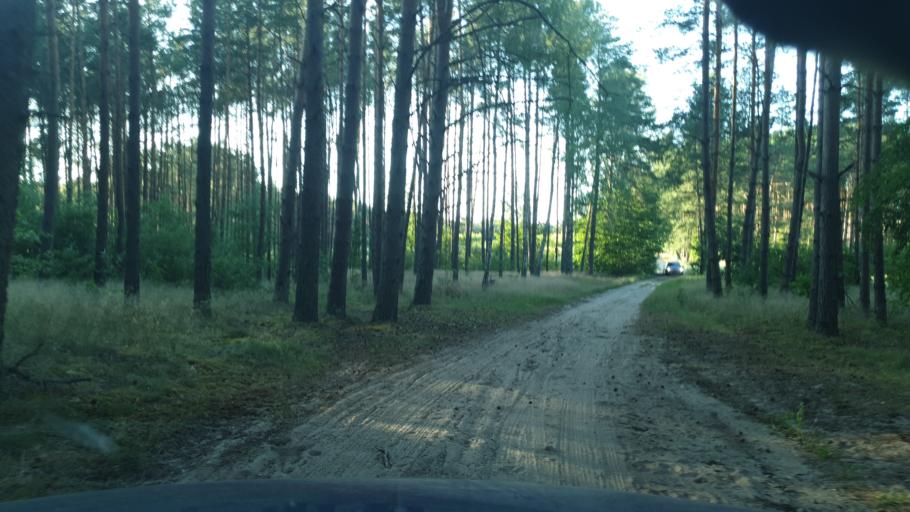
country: PL
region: Pomeranian Voivodeship
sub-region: Powiat bytowski
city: Lipnica
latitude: 53.8809
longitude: 17.4267
